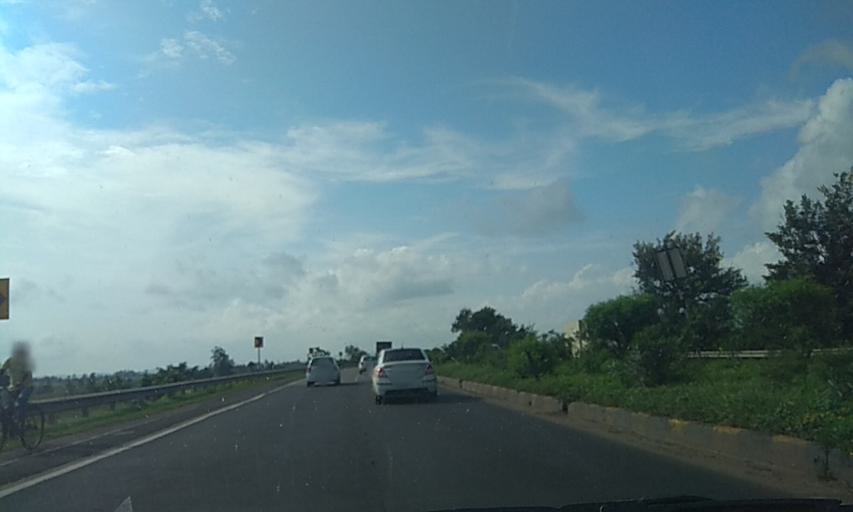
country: IN
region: Maharashtra
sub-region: Kolhapur
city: Kodoli
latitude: 16.8912
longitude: 74.2933
